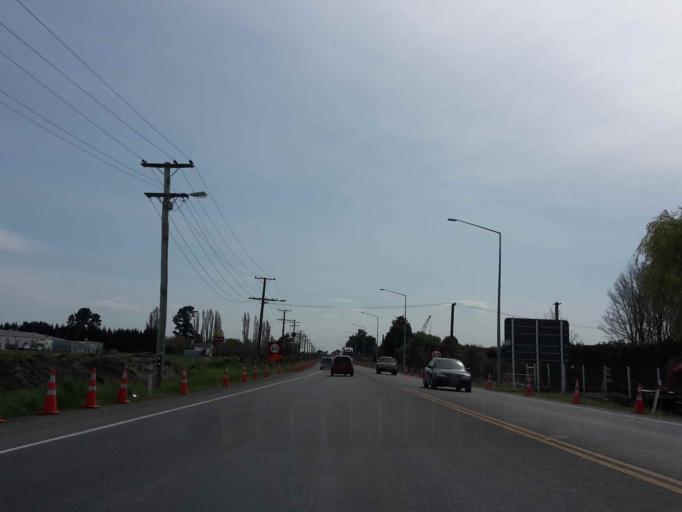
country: NZ
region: Canterbury
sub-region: Christchurch City
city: Christchurch
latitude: -43.4850
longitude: 172.5540
